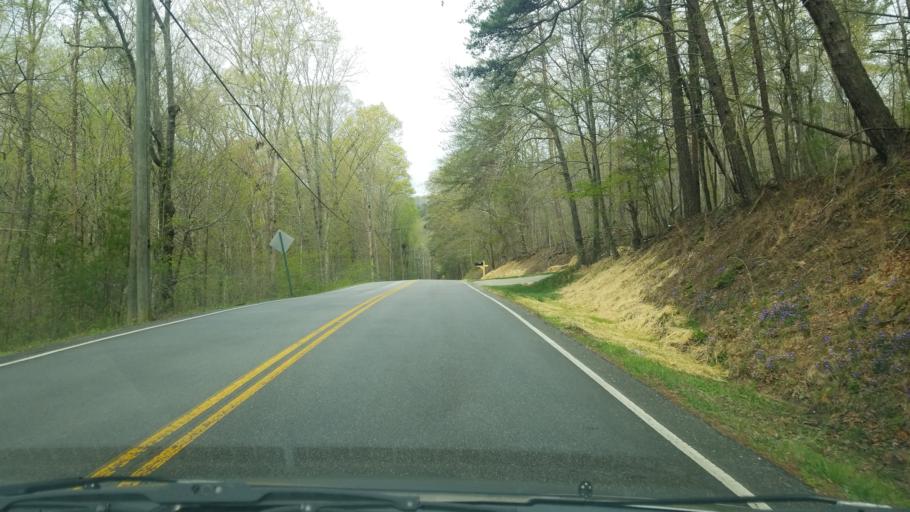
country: US
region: Tennessee
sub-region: Hamilton County
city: Collegedale
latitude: 35.0262
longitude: -85.0647
